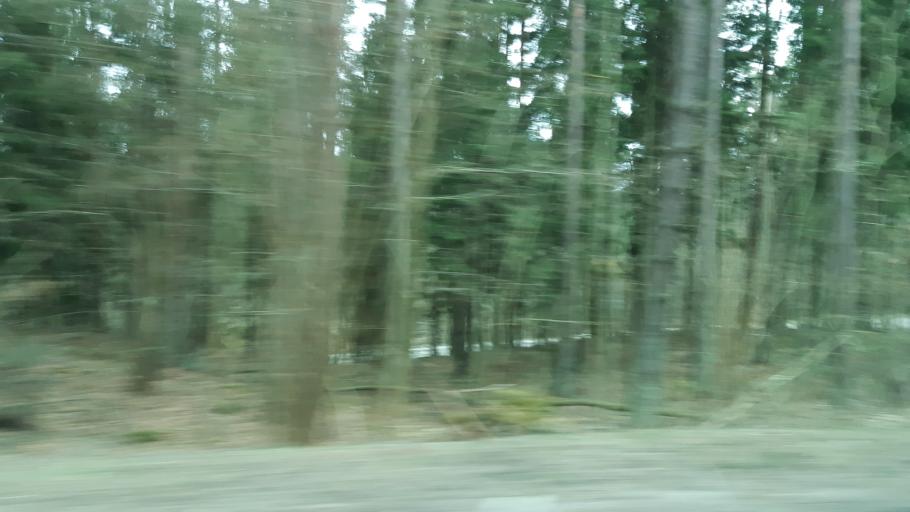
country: PL
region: Podlasie
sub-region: Suwalki
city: Suwalki
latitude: 54.3084
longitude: 22.9576
